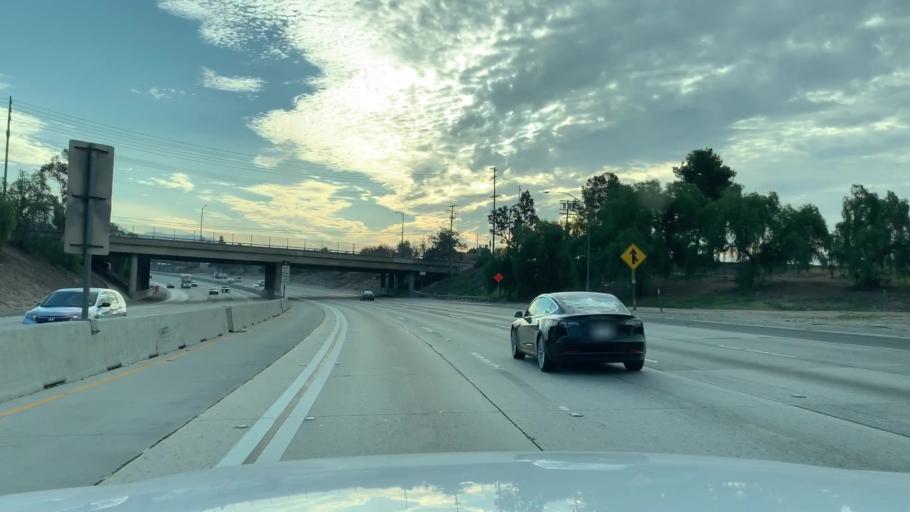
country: US
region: California
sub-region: Los Angeles County
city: North Hollywood
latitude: 34.2270
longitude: -118.3892
